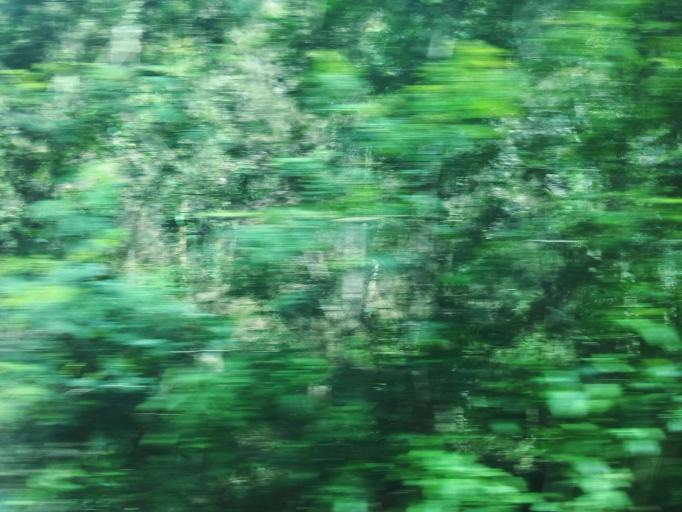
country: BR
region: Minas Gerais
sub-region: Caete
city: Caete
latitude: -19.8885
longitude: -43.7559
